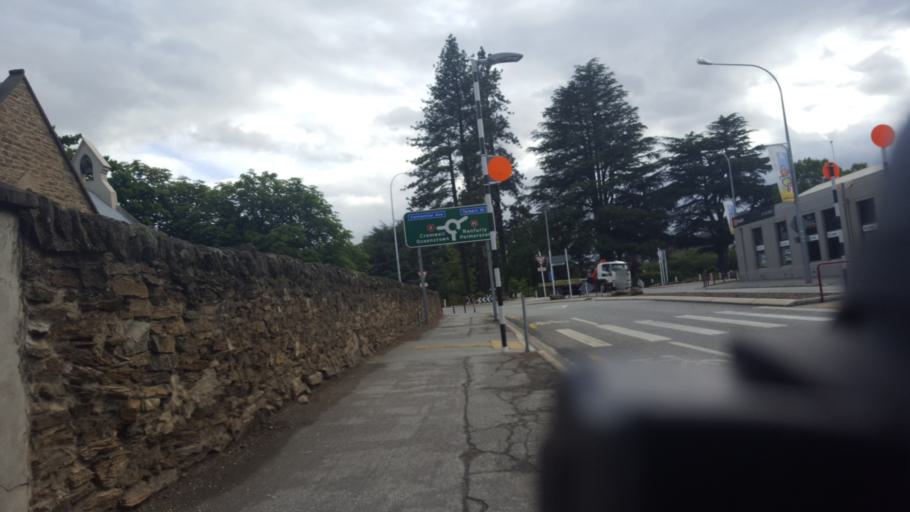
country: NZ
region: Otago
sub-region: Queenstown-Lakes District
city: Wanaka
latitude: -45.2555
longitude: 169.3916
